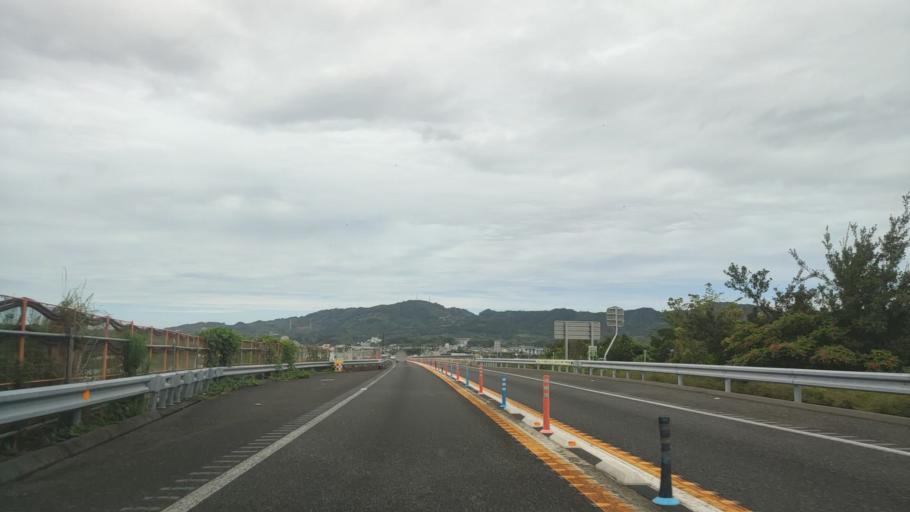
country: JP
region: Wakayama
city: Tanabe
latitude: 33.7743
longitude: 135.3365
